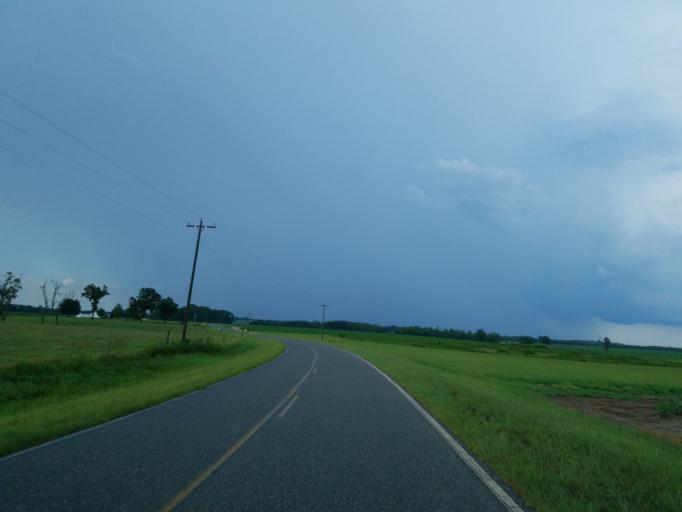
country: US
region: Georgia
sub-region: Cook County
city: Adel
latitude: 31.0682
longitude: -83.4438
